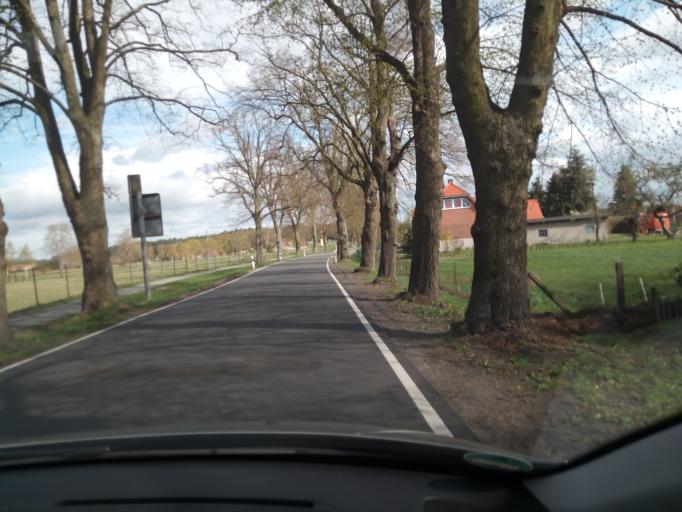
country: DE
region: Mecklenburg-Vorpommern
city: Boizenburg
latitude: 53.3987
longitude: 10.7484
